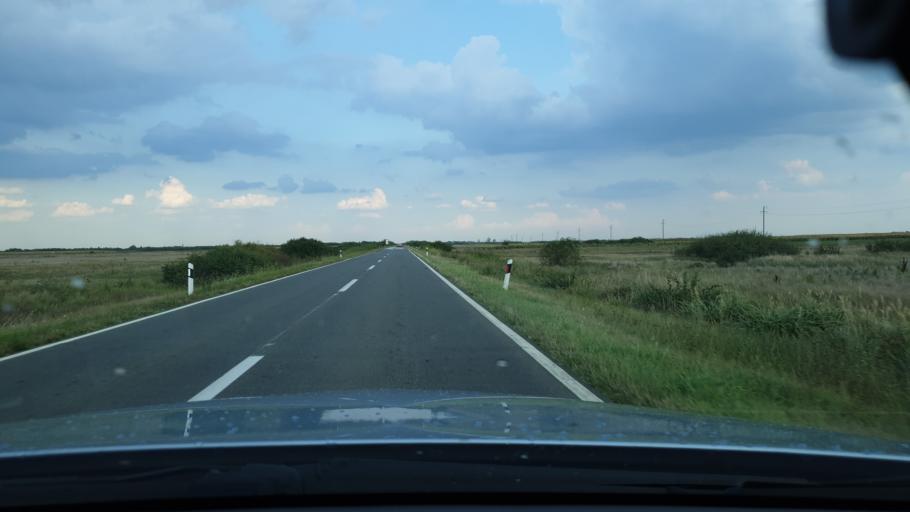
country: RS
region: Autonomna Pokrajina Vojvodina
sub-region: Srednjebanatski Okrug
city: Secanj
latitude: 45.3491
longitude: 20.7878
